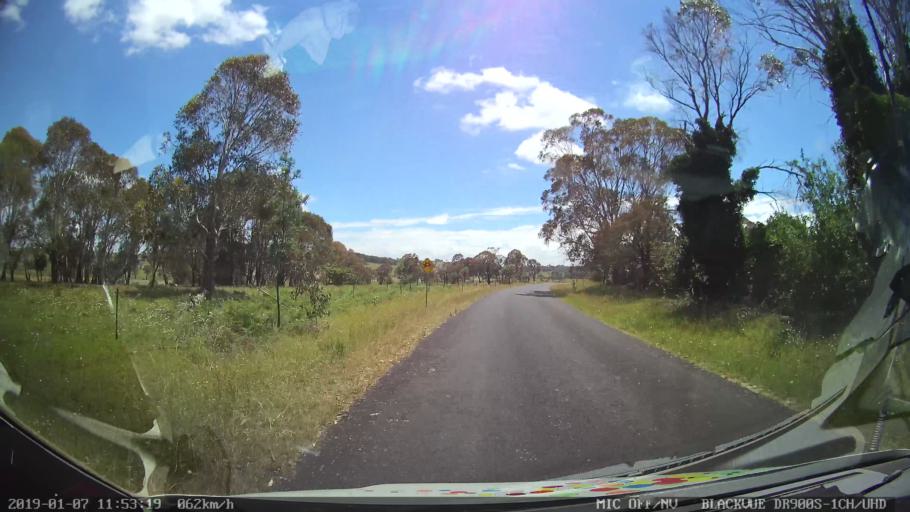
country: AU
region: New South Wales
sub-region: Guyra
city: Guyra
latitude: -30.3051
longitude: 151.6564
